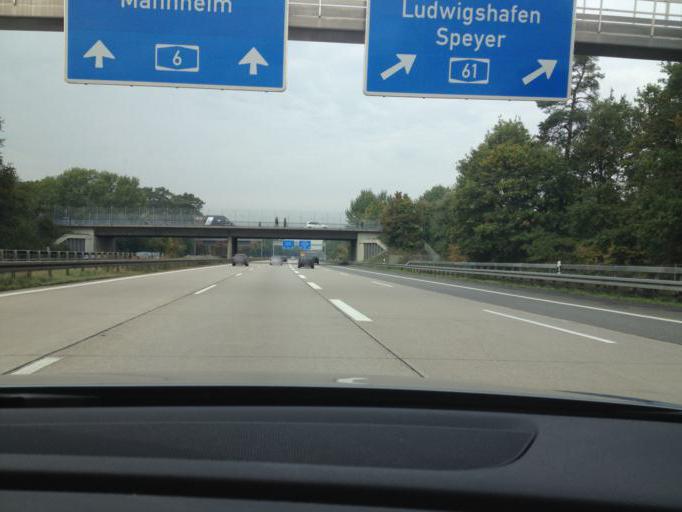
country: DE
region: Baden-Wuerttemberg
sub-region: Karlsruhe Region
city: Hockenheim
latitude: 49.3227
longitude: 8.5674
